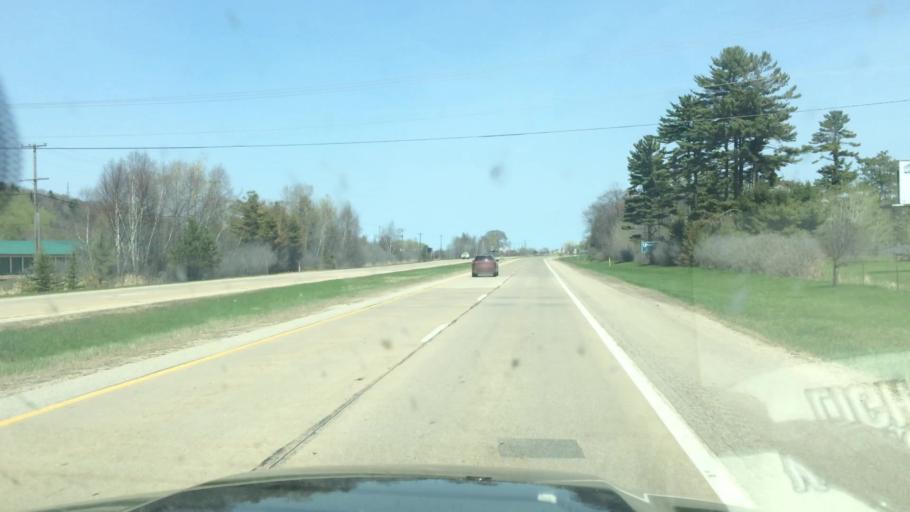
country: US
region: Michigan
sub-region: Delta County
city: Gladstone
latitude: 45.8381
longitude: -87.0374
